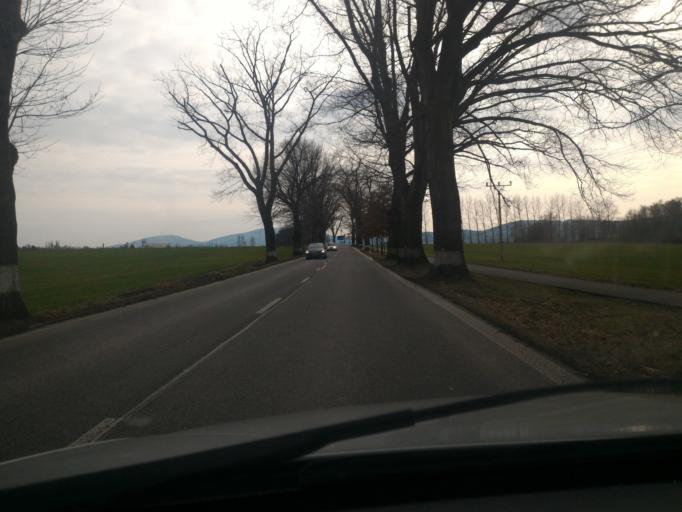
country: CZ
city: Hradek nad Nisou
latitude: 50.8695
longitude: 14.8300
